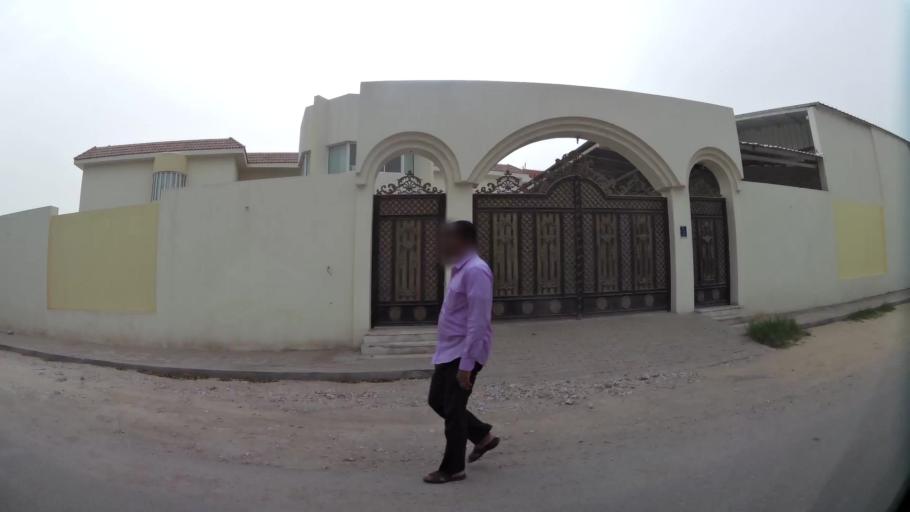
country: QA
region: Baladiyat ad Dawhah
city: Doha
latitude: 25.2579
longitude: 51.4932
